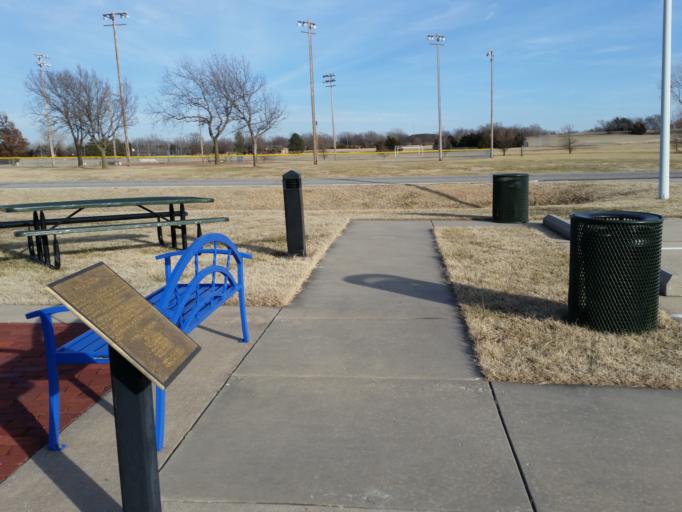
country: US
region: Kansas
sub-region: Harvey County
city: North Newton
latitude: 38.0616
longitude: -97.3371
